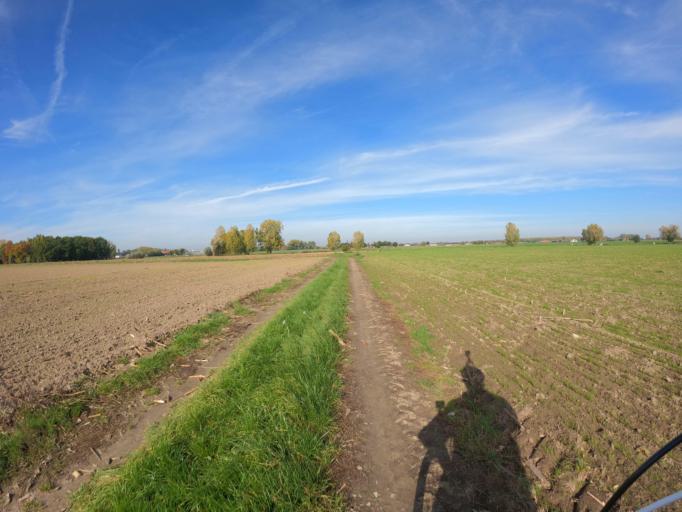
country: BE
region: Flanders
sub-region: Provincie West-Vlaanderen
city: Ruiselede
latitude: 51.0449
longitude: 3.3981
